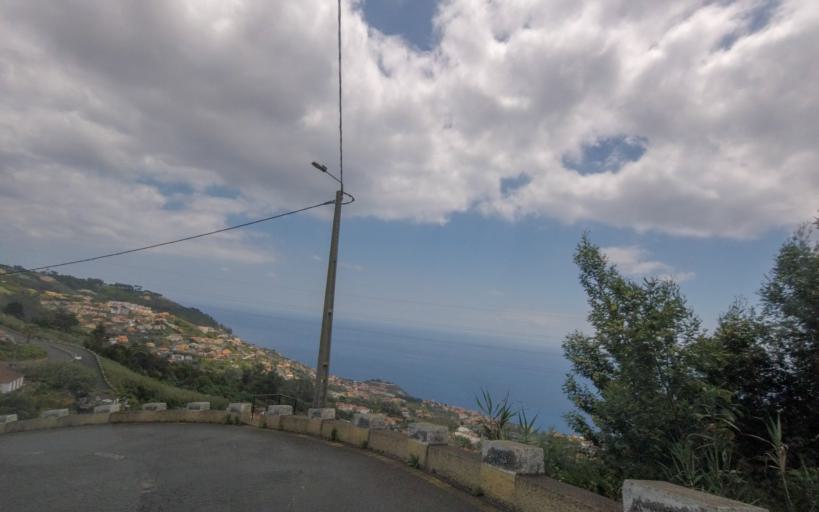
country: PT
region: Madeira
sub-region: Funchal
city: Nossa Senhora do Monte
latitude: 32.6645
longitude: -16.8822
